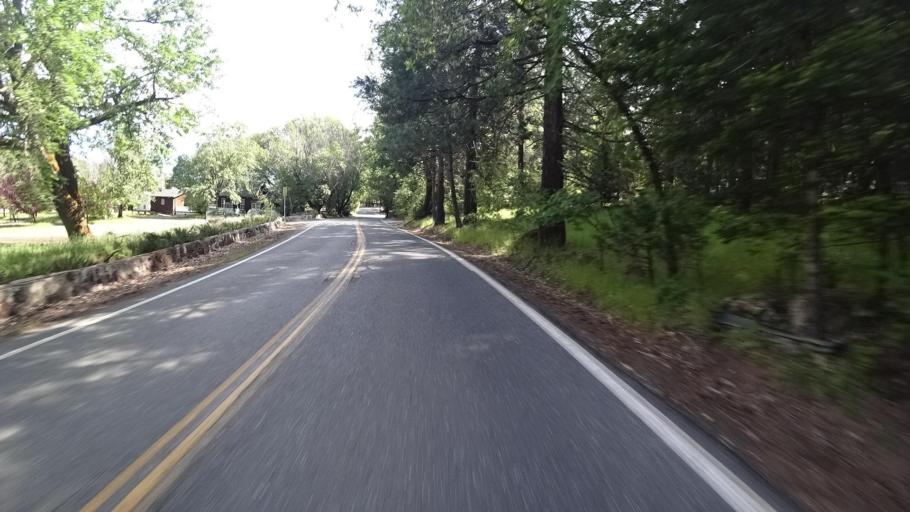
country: US
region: California
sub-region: Lake County
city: Cobb
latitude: 38.8755
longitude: -122.7291
